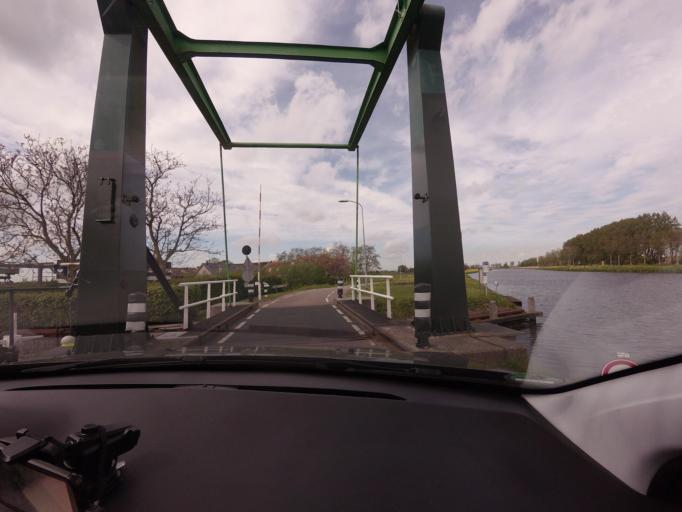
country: NL
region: North Holland
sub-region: Gemeente Beemster
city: Halfweg
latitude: 52.5213
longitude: 4.8694
